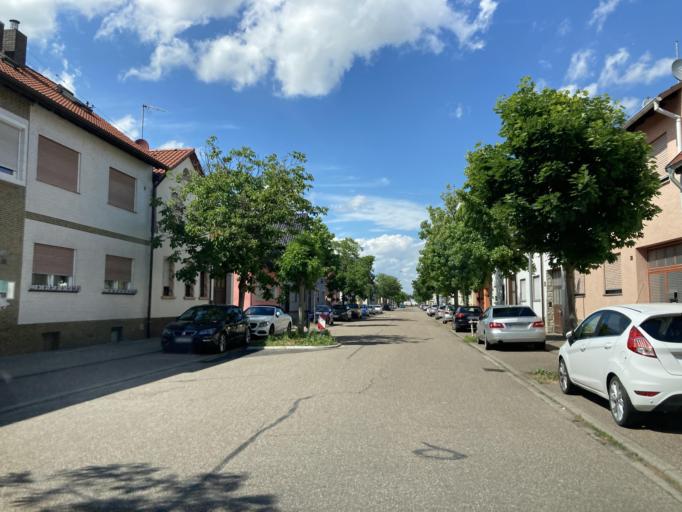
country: DE
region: Baden-Wuerttemberg
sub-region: Karlsruhe Region
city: Philippsburg
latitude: 49.1986
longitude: 8.4681
